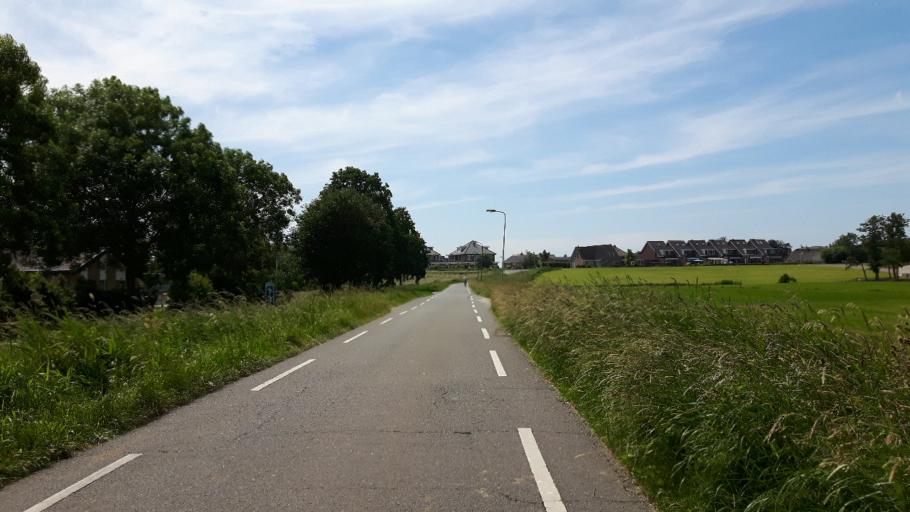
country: NL
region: South Holland
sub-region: Gemeente Nieuwkoop
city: Nieuwkoop
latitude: 52.1393
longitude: 4.7349
